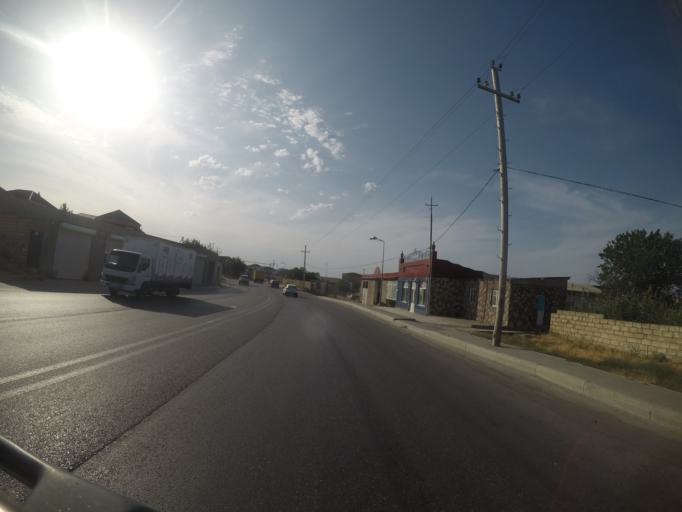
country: AZ
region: Baki
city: Binagadi
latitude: 40.4733
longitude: 49.8351
